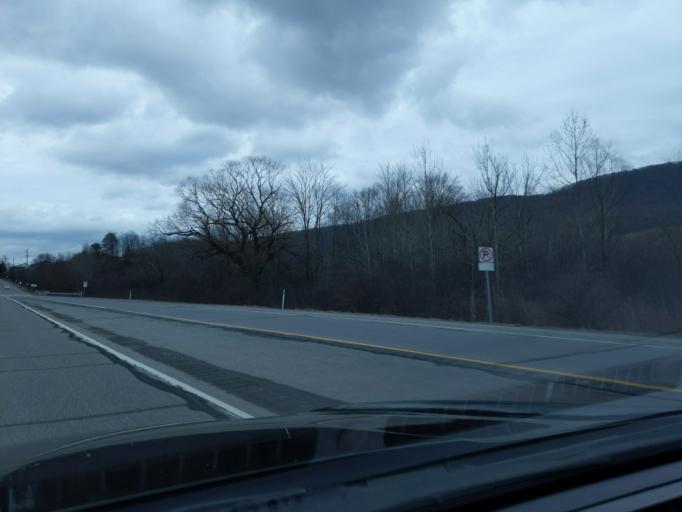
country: US
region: Pennsylvania
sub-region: Blair County
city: Tipton
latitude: 40.6454
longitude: -78.2744
